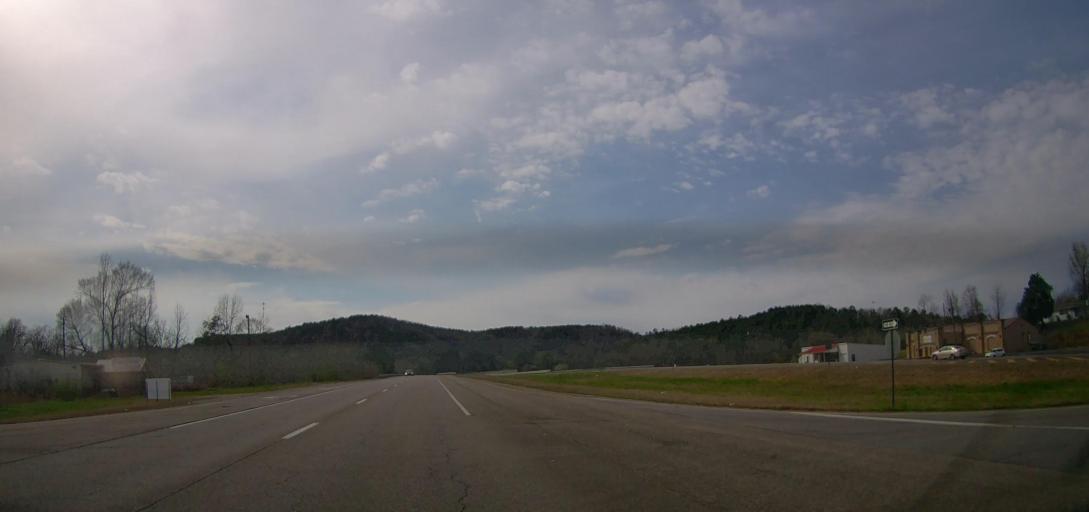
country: US
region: Alabama
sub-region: Walker County
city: Cordova
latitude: 33.8058
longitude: -87.1367
